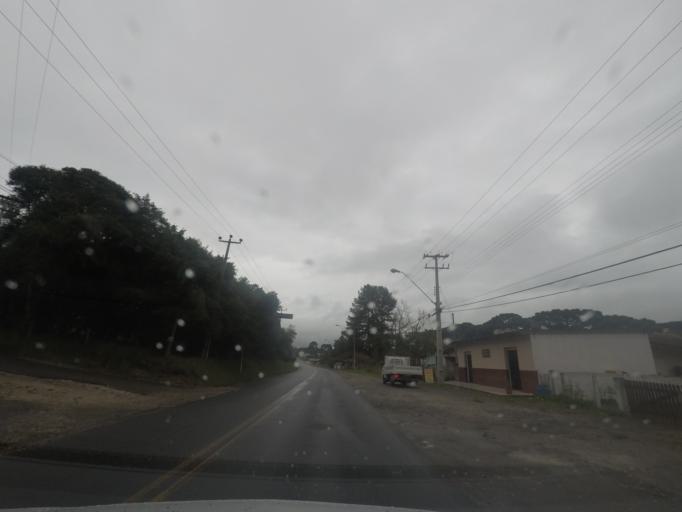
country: BR
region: Parana
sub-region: Campina Grande Do Sul
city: Campina Grande do Sul
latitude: -25.3158
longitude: -49.0742
